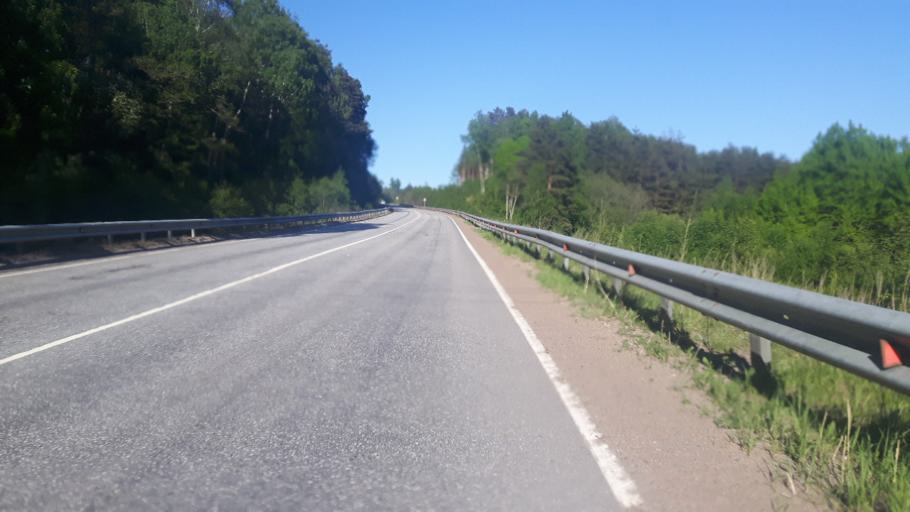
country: RU
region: Leningrad
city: Sosnovyy Bor
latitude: 60.1680
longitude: 29.1830
